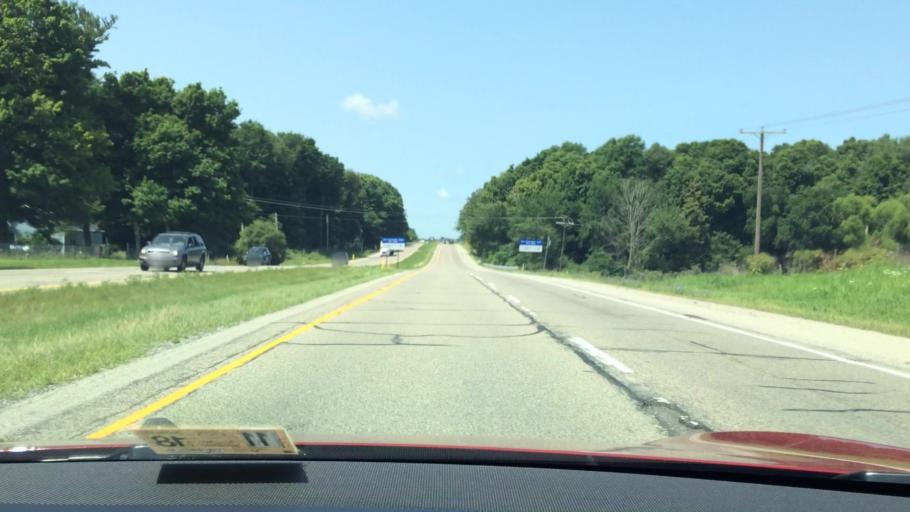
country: US
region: Indiana
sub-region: LaPorte County
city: Hudson Lake
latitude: 41.6728
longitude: -86.5732
